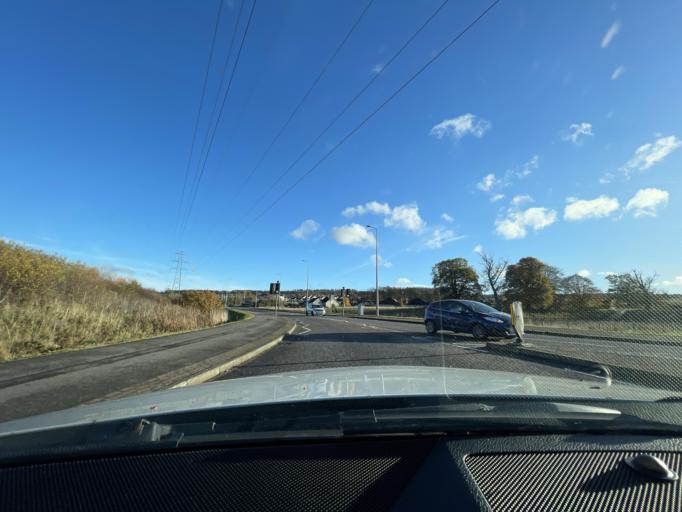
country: GB
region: Scotland
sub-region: Highland
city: Inverness
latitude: 57.4475
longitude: -4.2325
